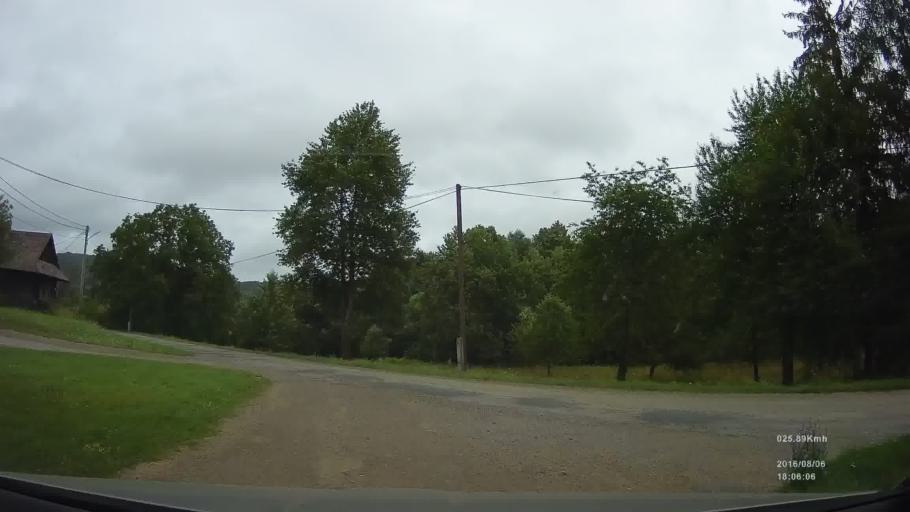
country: SK
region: Presovsky
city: Svidnik
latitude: 49.4038
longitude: 21.5675
